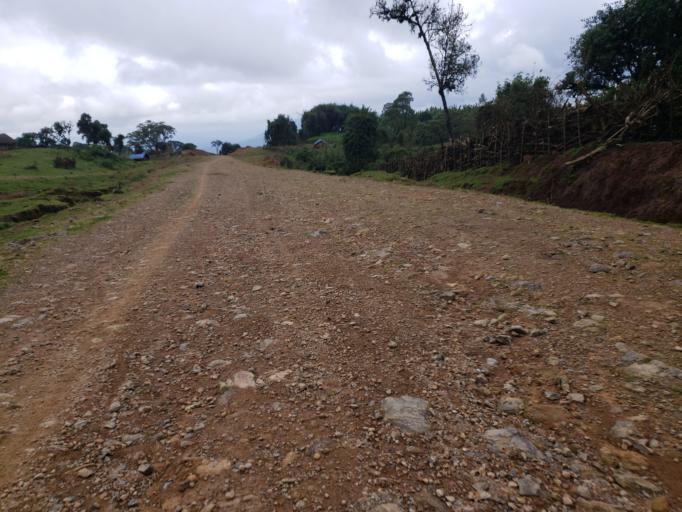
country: ET
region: Oromiya
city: Dodola
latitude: 6.6908
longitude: 39.3693
